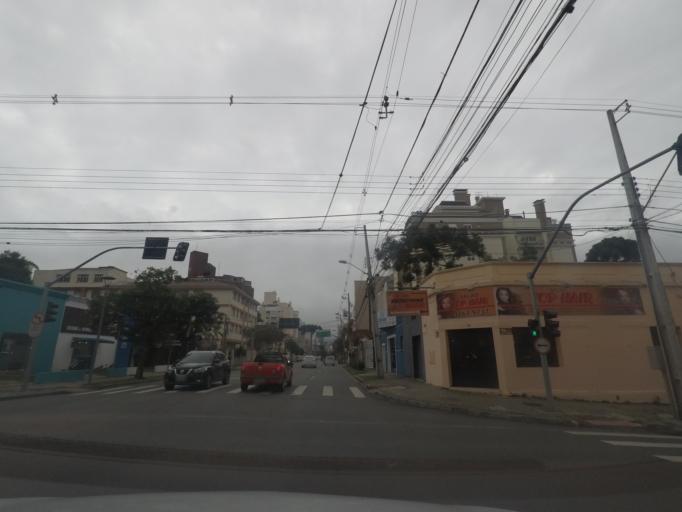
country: BR
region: Parana
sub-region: Curitiba
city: Curitiba
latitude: -25.4295
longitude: -49.2564
